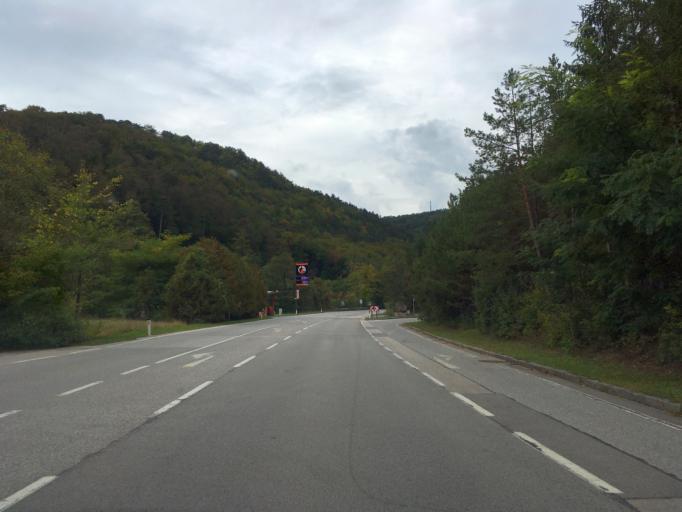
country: AT
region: Lower Austria
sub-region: Politischer Bezirk Modling
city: Gaaden
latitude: 48.0640
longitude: 16.2154
